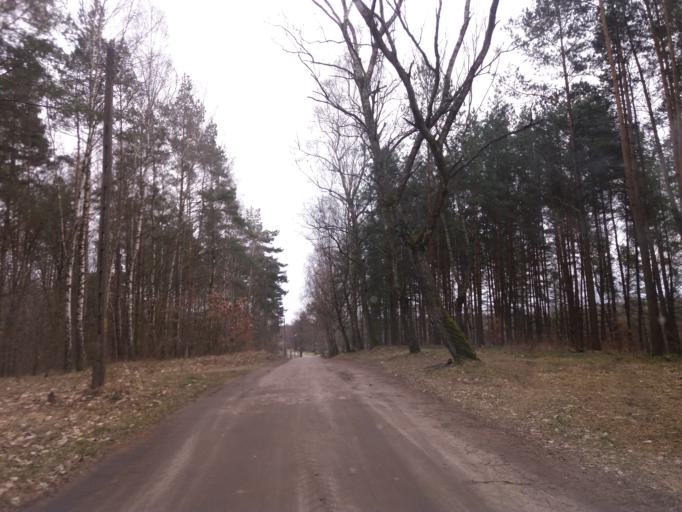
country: PL
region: West Pomeranian Voivodeship
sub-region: Powiat choszczenski
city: Drawno
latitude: 53.2162
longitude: 15.7240
